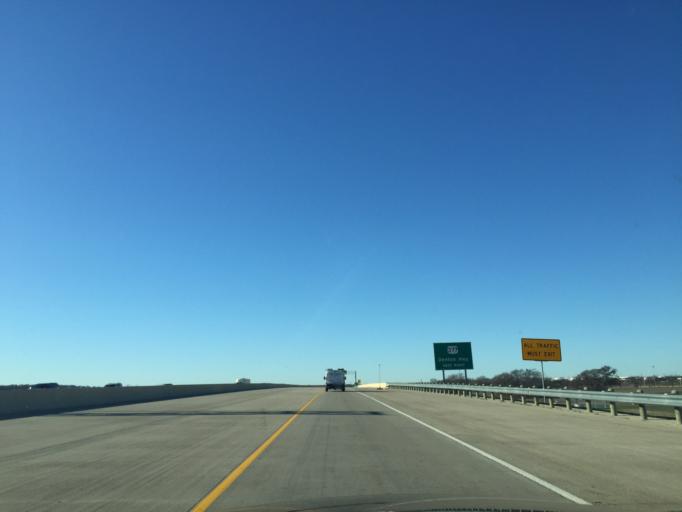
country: US
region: Texas
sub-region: Denton County
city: Roanoke
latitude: 32.9931
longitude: -97.2223
